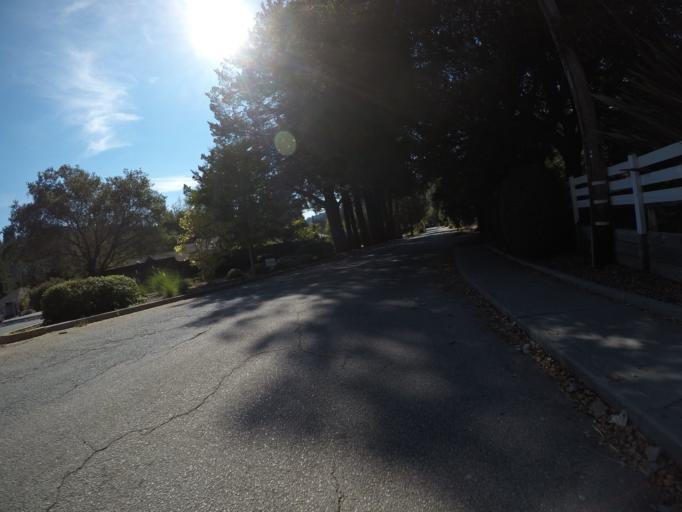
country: US
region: California
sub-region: Santa Cruz County
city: Scotts Valley
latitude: 37.0559
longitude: -121.9975
